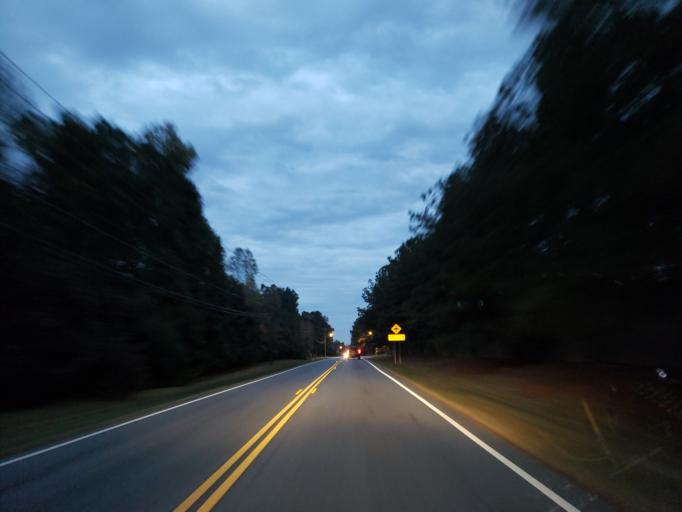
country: US
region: Georgia
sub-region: Cobb County
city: Powder Springs
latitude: 33.9282
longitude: -84.6973
